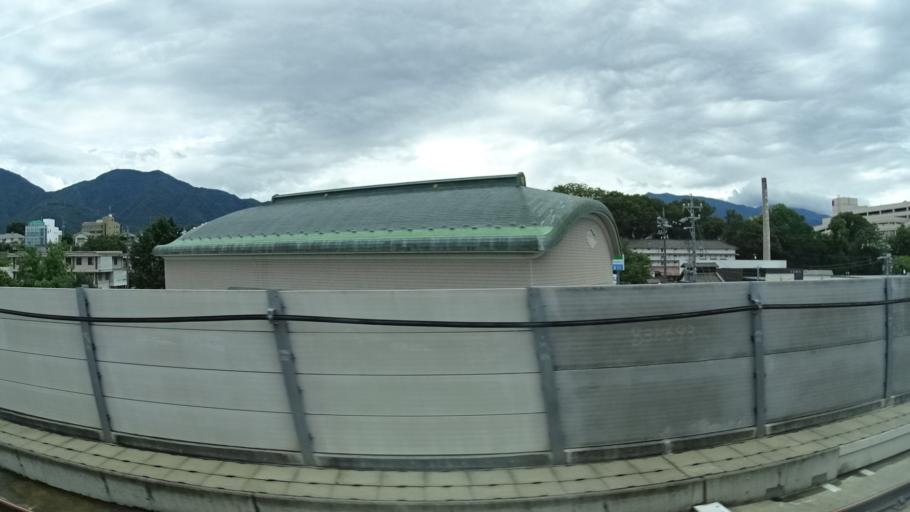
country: JP
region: Nagano
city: Ueda
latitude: 36.3991
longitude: 138.2467
